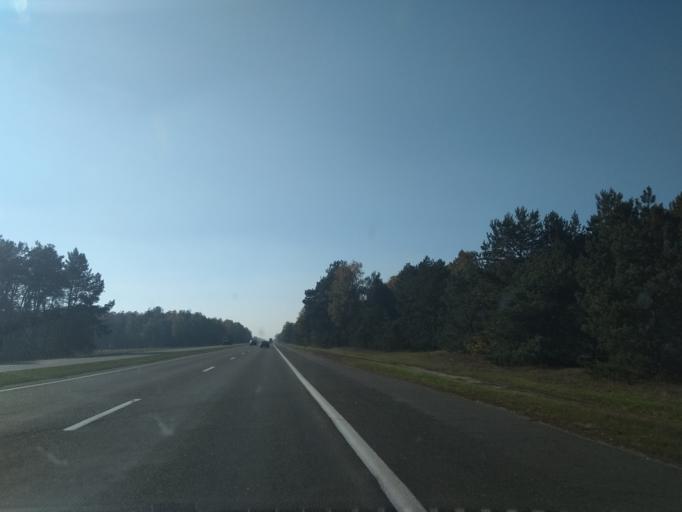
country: BY
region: Brest
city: Zhabinka
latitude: 52.1776
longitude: 24.1663
